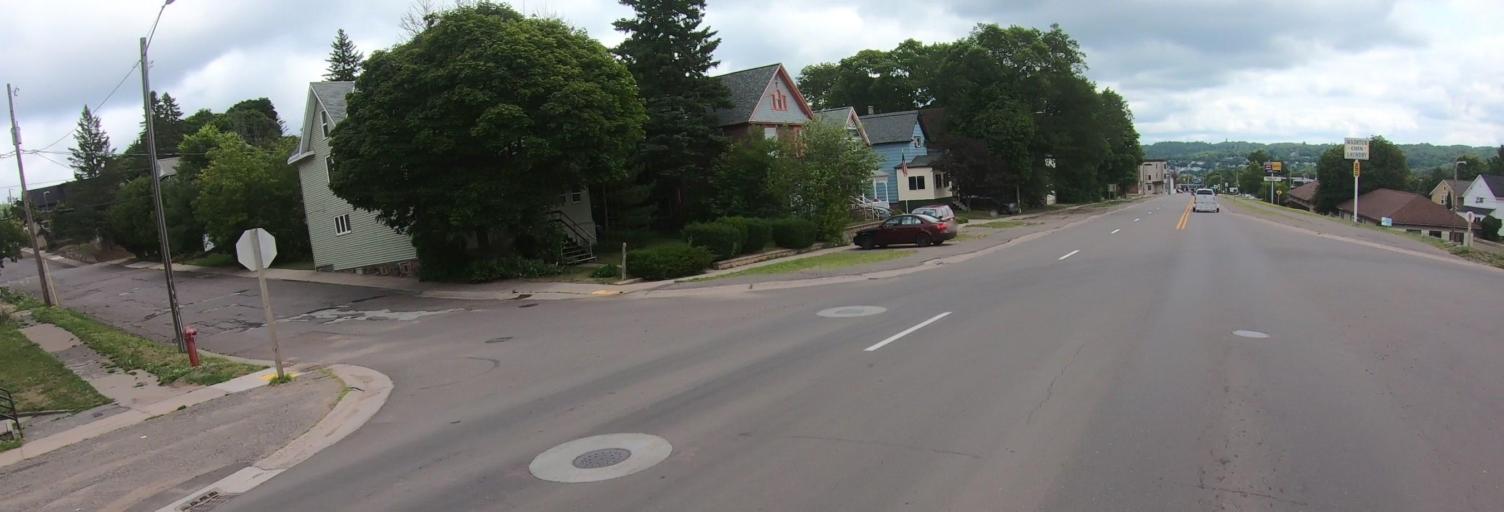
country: US
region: Michigan
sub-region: Houghton County
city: Hancock
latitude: 47.1285
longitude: -88.5977
